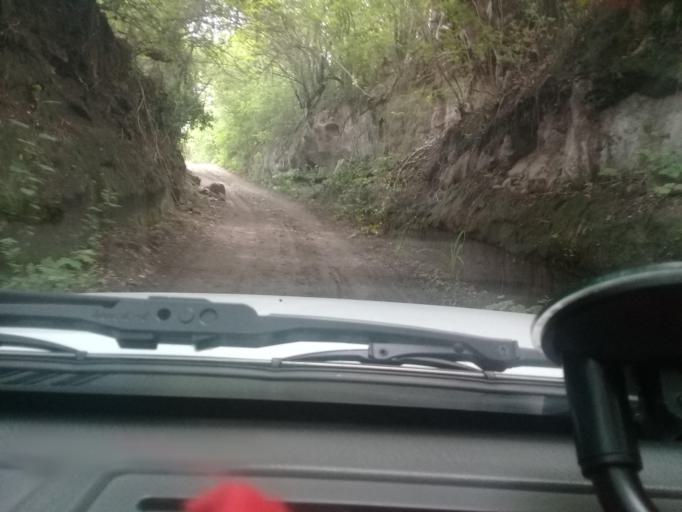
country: MX
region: Veracruz
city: Paso de Ovejas
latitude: 19.2842
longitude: -96.4285
